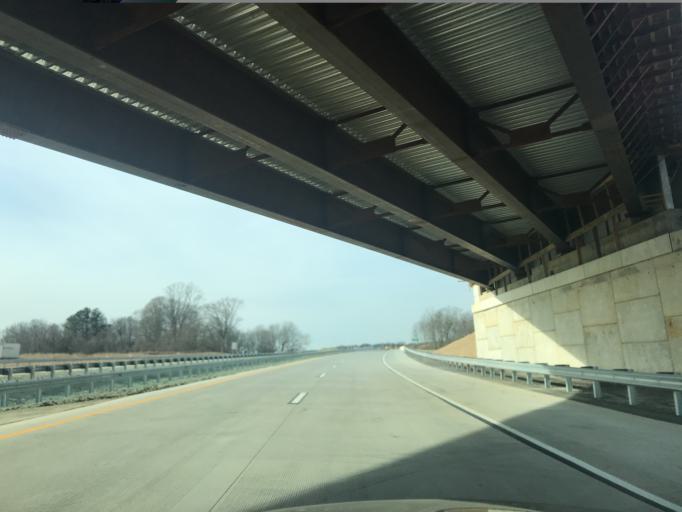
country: US
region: Delaware
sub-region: New Castle County
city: Delaware City
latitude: 39.5245
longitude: -75.6633
